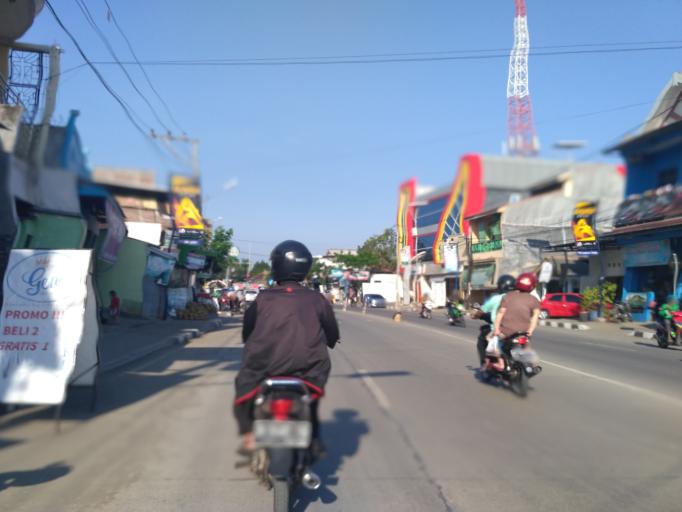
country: ID
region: Central Java
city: Semarang
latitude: -6.9857
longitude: 110.4471
